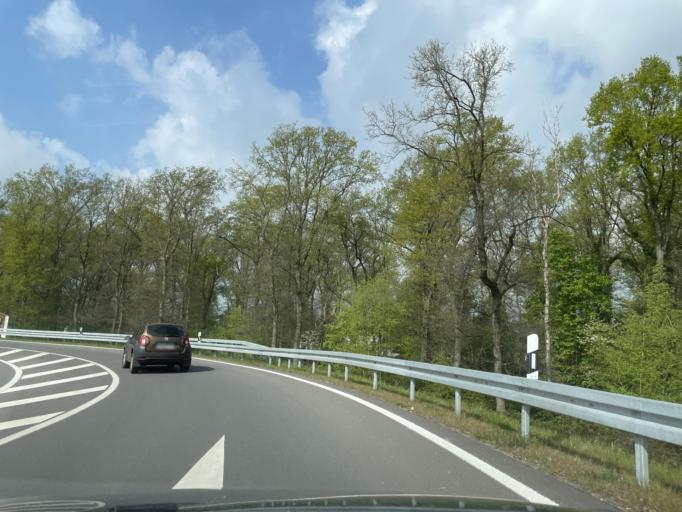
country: DE
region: North Rhine-Westphalia
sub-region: Regierungsbezirk Dusseldorf
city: Hochfeld
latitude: 51.3529
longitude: 6.7422
